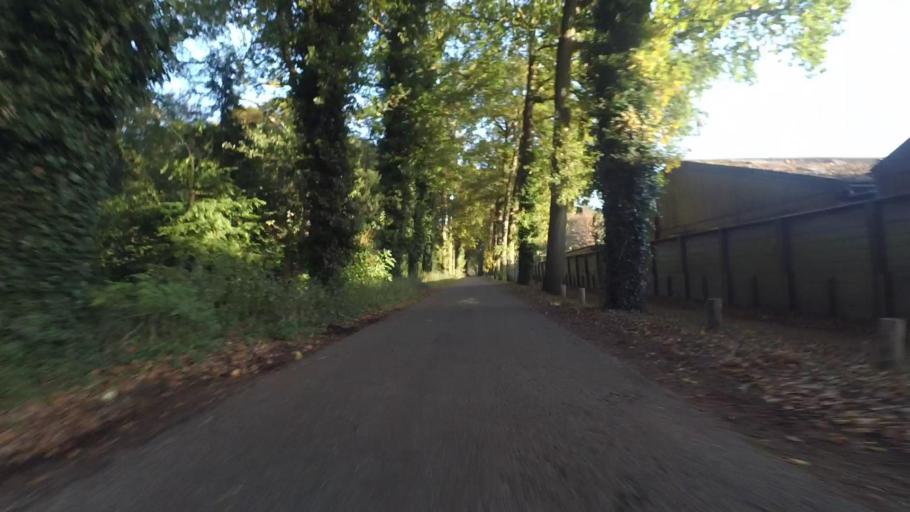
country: NL
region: Utrecht
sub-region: Gemeente De Bilt
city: De Bilt
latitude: 52.1615
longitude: 5.2006
